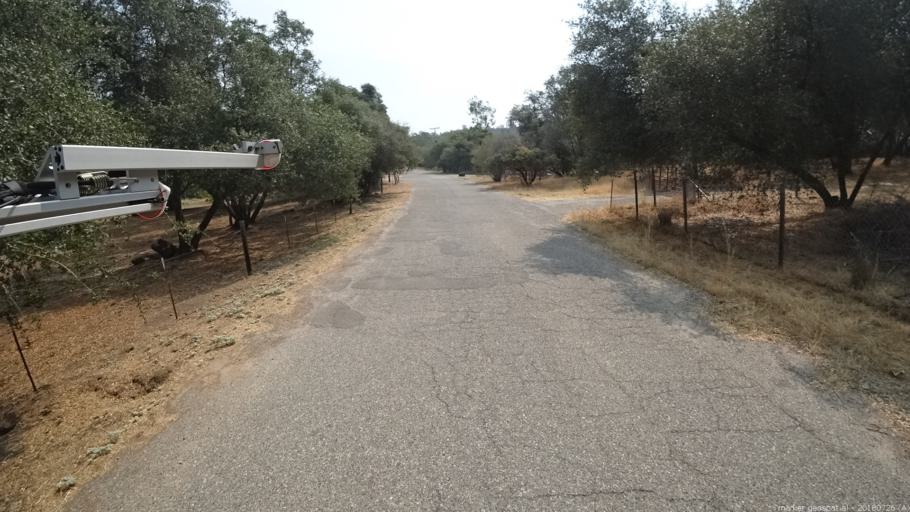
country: US
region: California
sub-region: Madera County
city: Coarsegold
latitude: 37.2362
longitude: -119.7008
